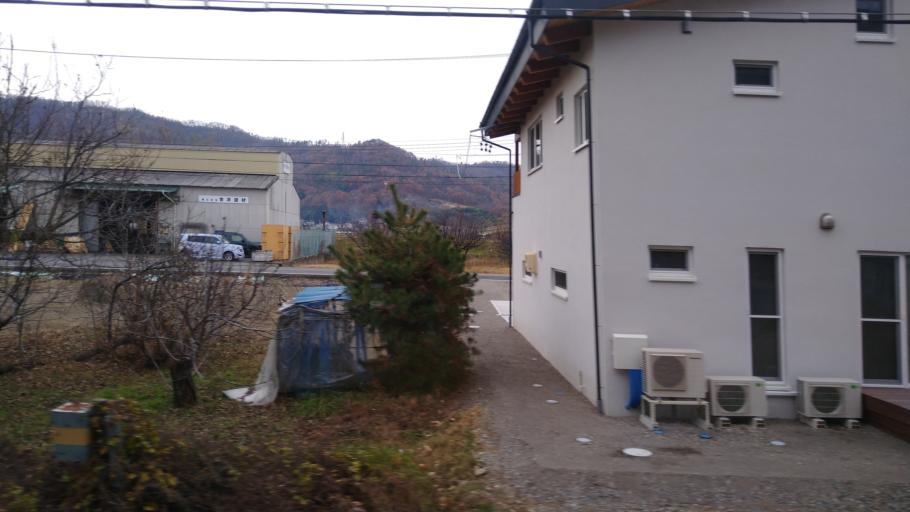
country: JP
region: Nagano
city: Ueda
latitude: 36.3900
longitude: 138.2570
